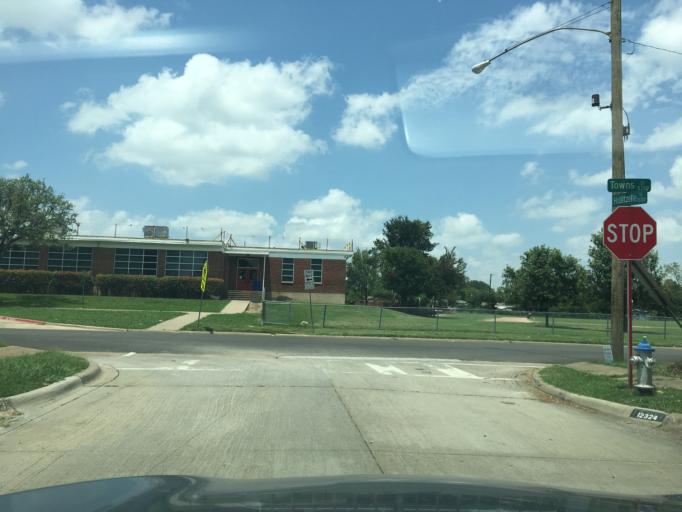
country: US
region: Texas
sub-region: Dallas County
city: Richardson
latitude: 32.9164
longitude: -96.7585
